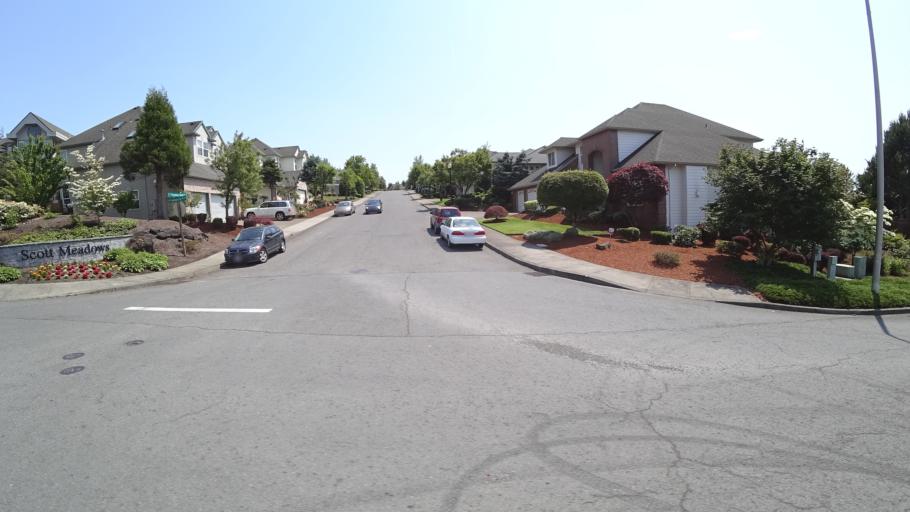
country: US
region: Oregon
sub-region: Multnomah County
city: Lents
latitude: 45.4563
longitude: -122.5618
